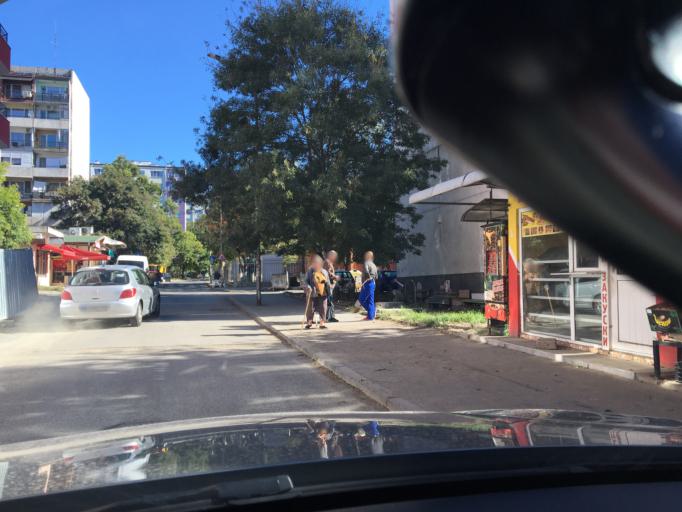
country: BG
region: Burgas
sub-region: Obshtina Burgas
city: Burgas
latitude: 42.5183
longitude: 27.4470
